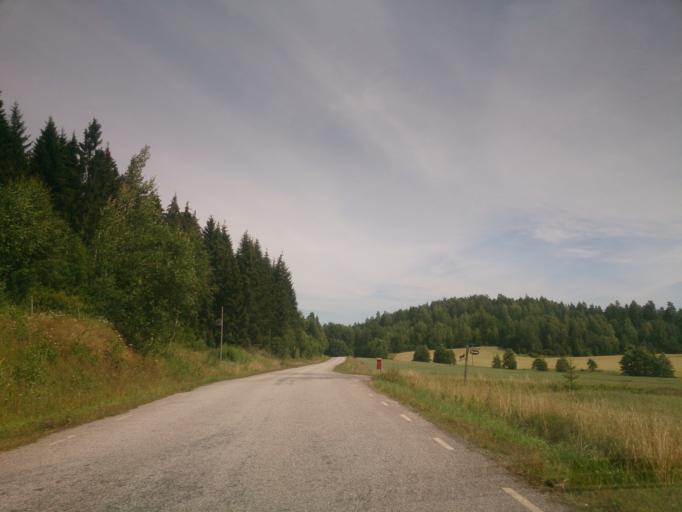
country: SE
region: OEstergoetland
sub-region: Valdemarsviks Kommun
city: Gusum
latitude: 58.3381
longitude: 16.5853
